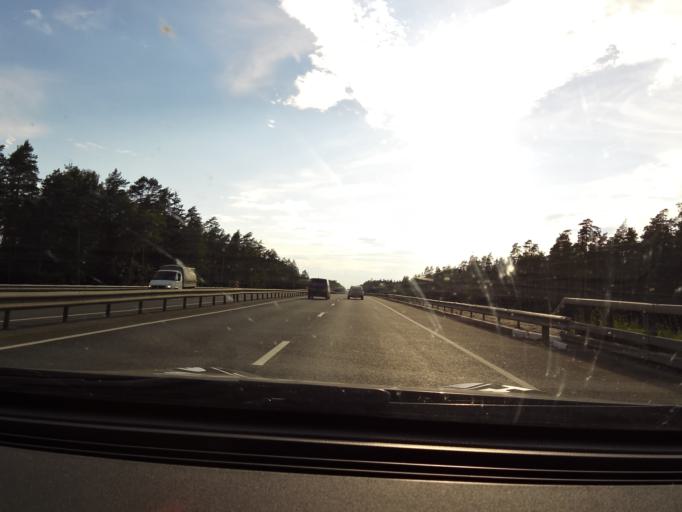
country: RU
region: Vladimir
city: Krasnyy Oktyabr'
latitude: 56.2177
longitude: 41.4471
